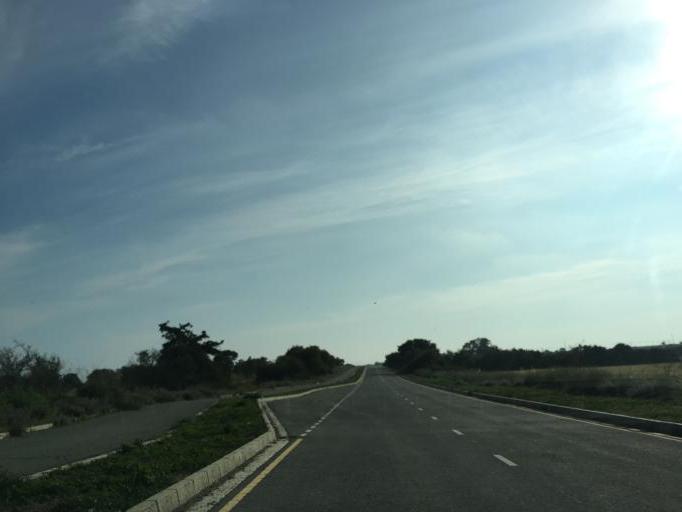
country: CY
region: Larnaka
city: Tersefanou
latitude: 34.7889
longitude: 33.4982
